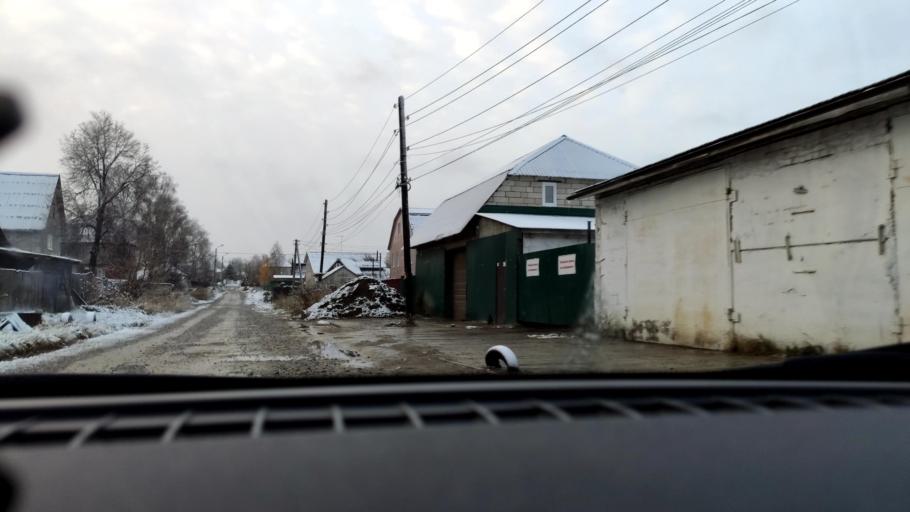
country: RU
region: Perm
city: Kondratovo
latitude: 58.0483
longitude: 56.0424
